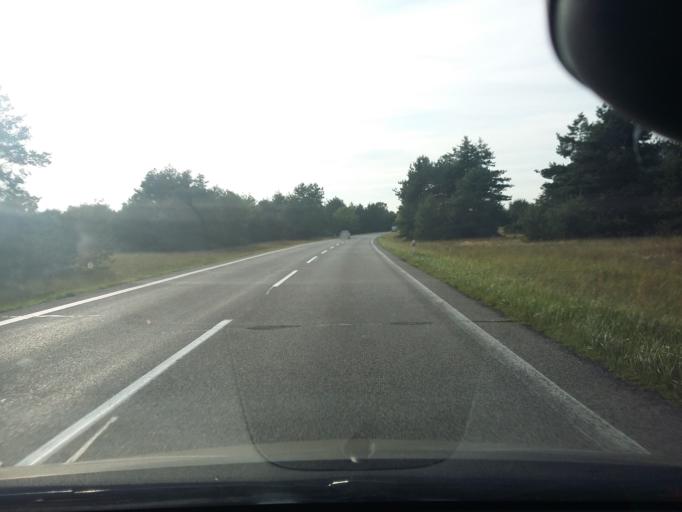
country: SK
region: Bratislavsky
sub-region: Okres Malacky
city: Malacky
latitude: 48.4080
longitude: 17.0741
